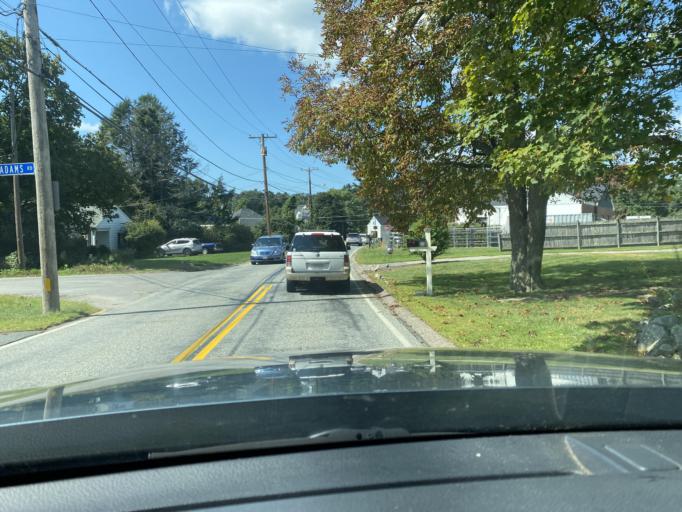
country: US
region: Massachusetts
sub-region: Norfolk County
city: Walpole
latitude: 42.1655
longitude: -71.2306
